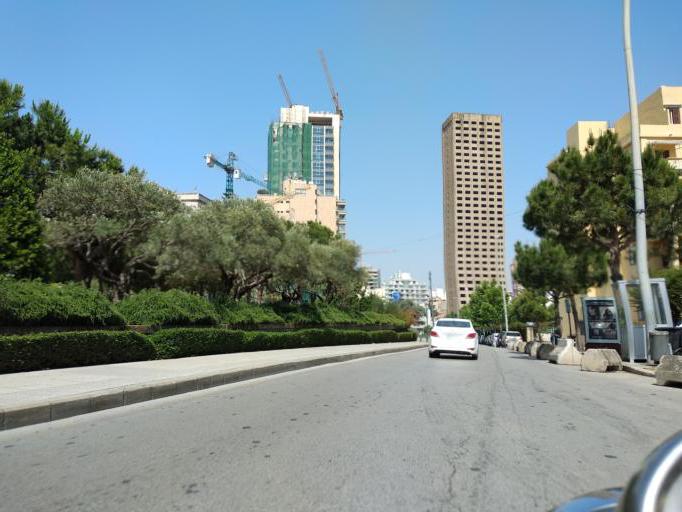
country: LB
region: Beyrouth
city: Beirut
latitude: 33.8946
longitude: 35.4991
